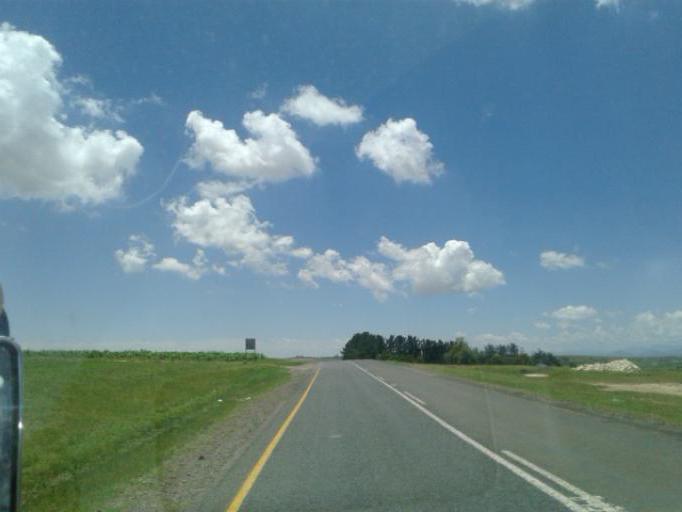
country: LS
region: Maseru
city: Maseru
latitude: -29.2980
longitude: 27.6154
